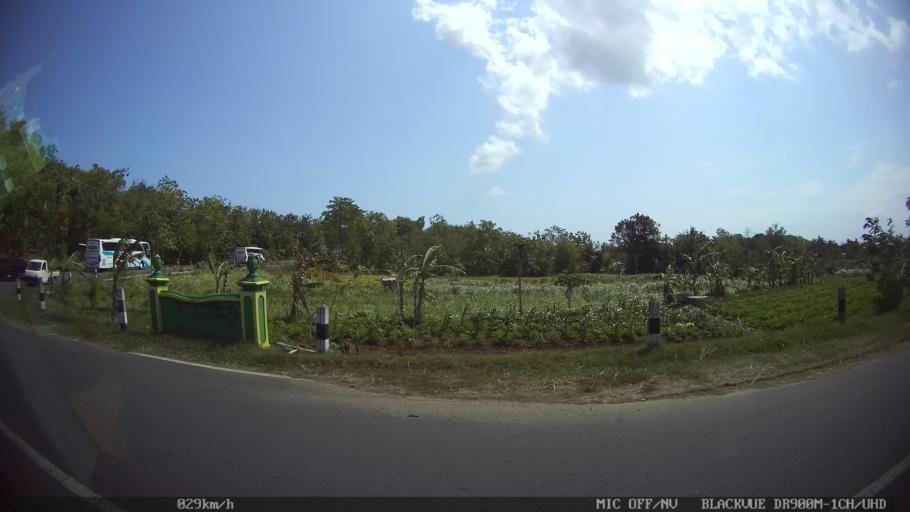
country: ID
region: Daerah Istimewa Yogyakarta
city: Pundong
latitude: -7.9764
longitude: 110.3473
